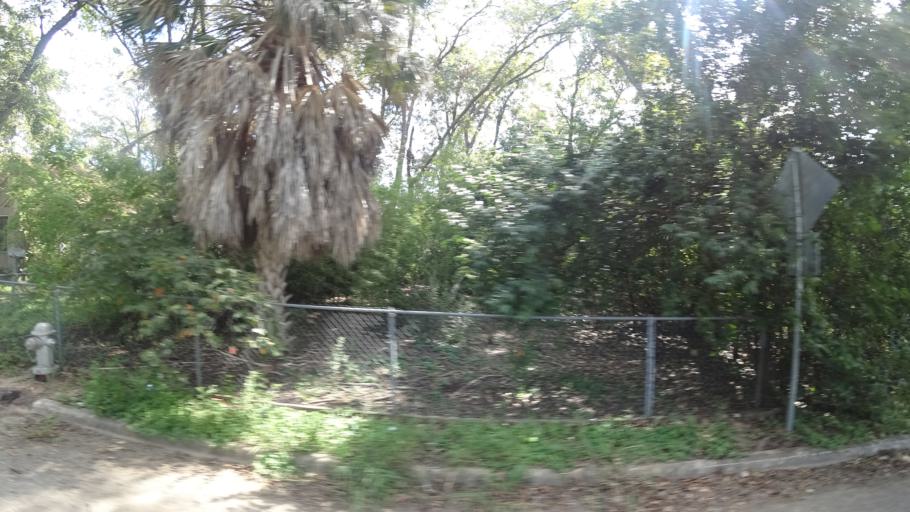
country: US
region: Texas
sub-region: Travis County
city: Austin
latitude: 30.2597
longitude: -97.7027
